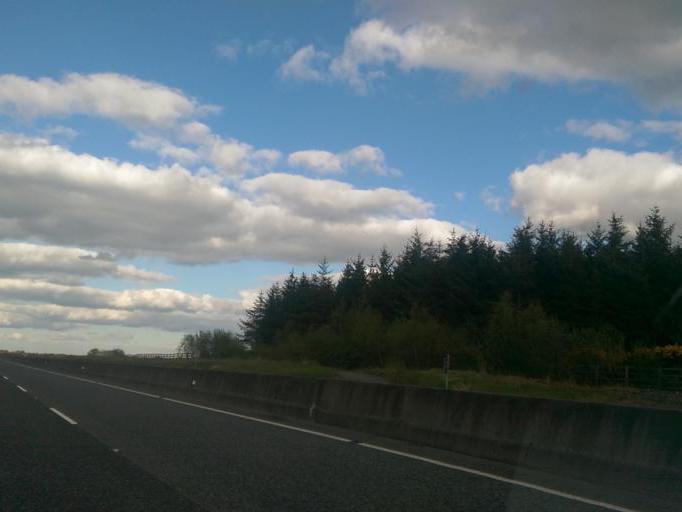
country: IE
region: Leinster
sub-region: An Iarmhi
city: Rochfortbridge
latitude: 53.4150
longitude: -7.2637
